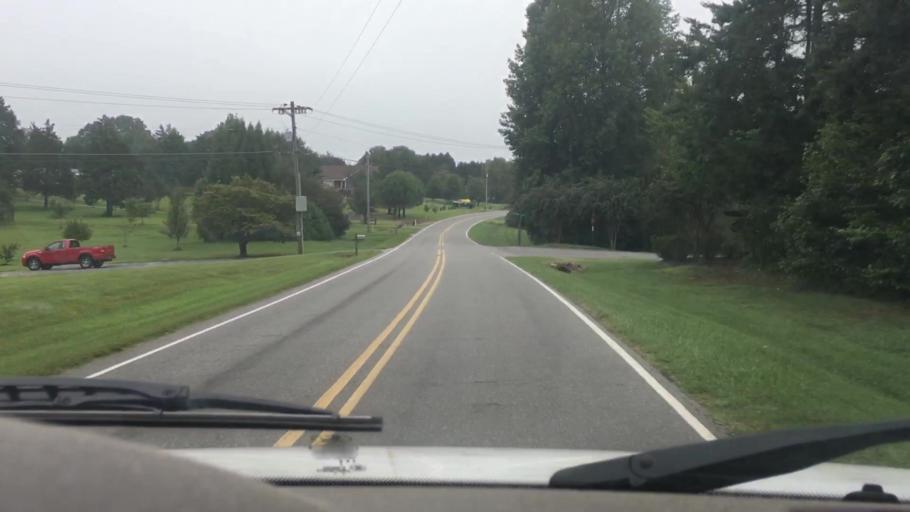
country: US
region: North Carolina
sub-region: Gaston County
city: Davidson
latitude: 35.5227
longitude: -80.7994
